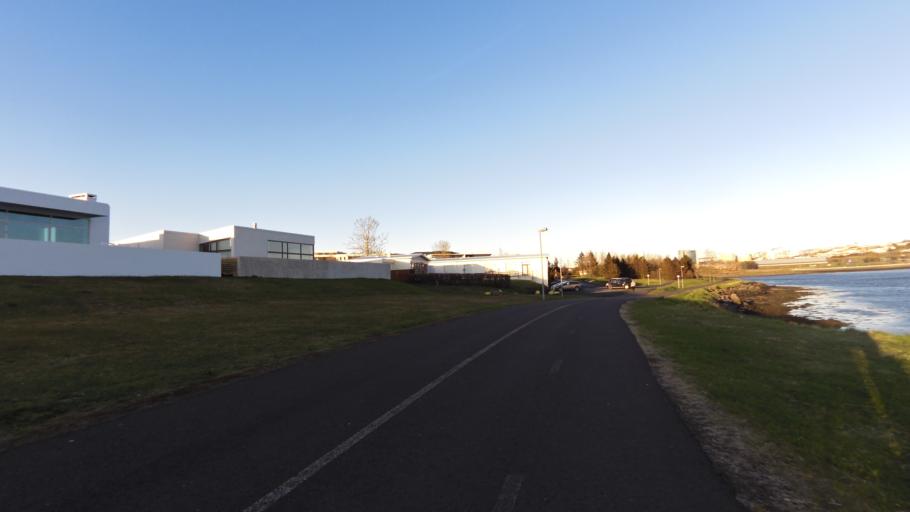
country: IS
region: Capital Region
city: Kopavogur
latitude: 64.1069
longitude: -21.9170
